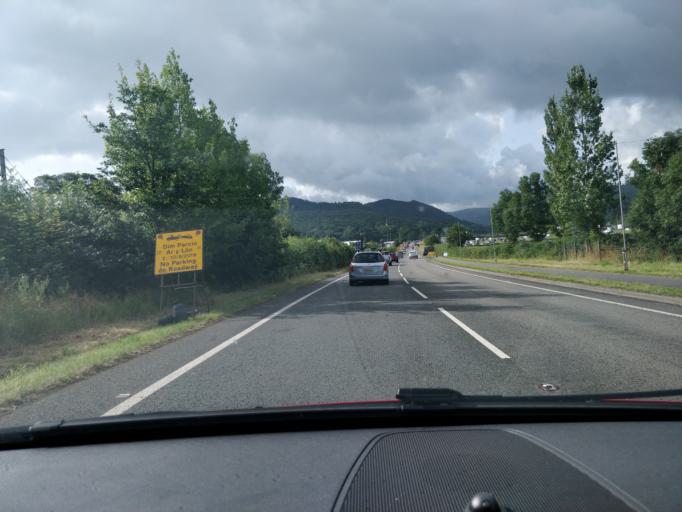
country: GB
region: Wales
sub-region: Conwy
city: Llanrwst
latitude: 53.1173
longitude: -3.7808
